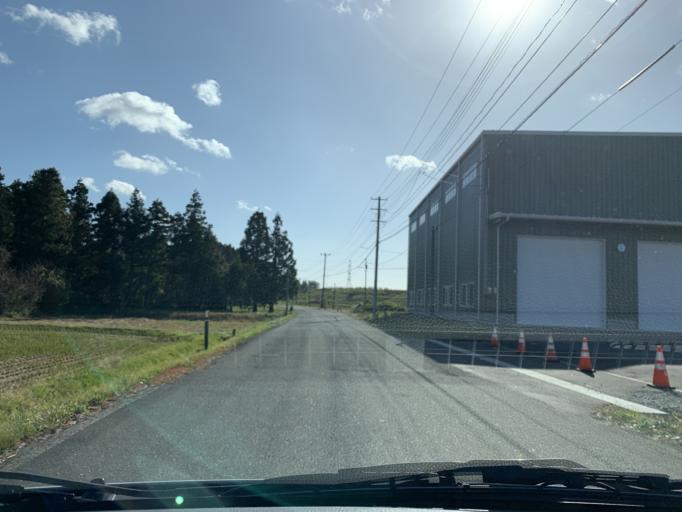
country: JP
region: Iwate
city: Mizusawa
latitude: 39.0296
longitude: 141.1209
